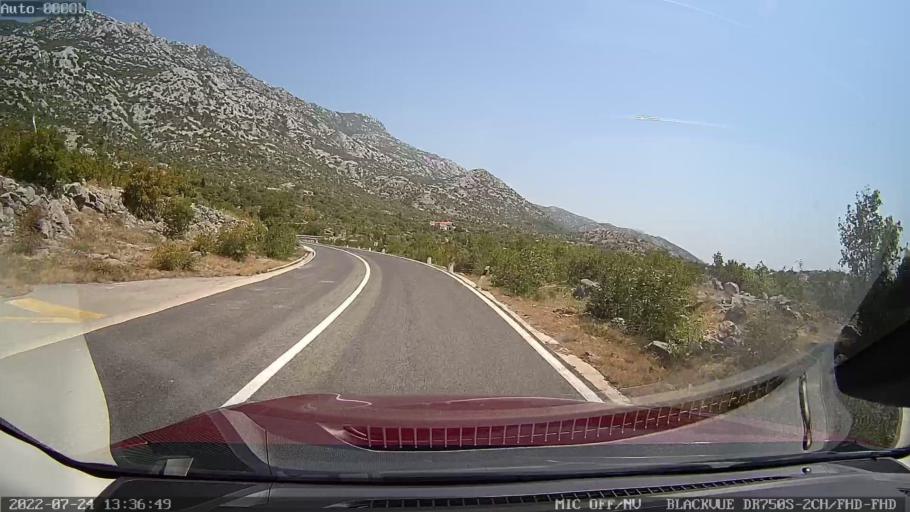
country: HR
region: Licko-Senjska
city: Karlobag
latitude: 44.5626
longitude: 15.0267
